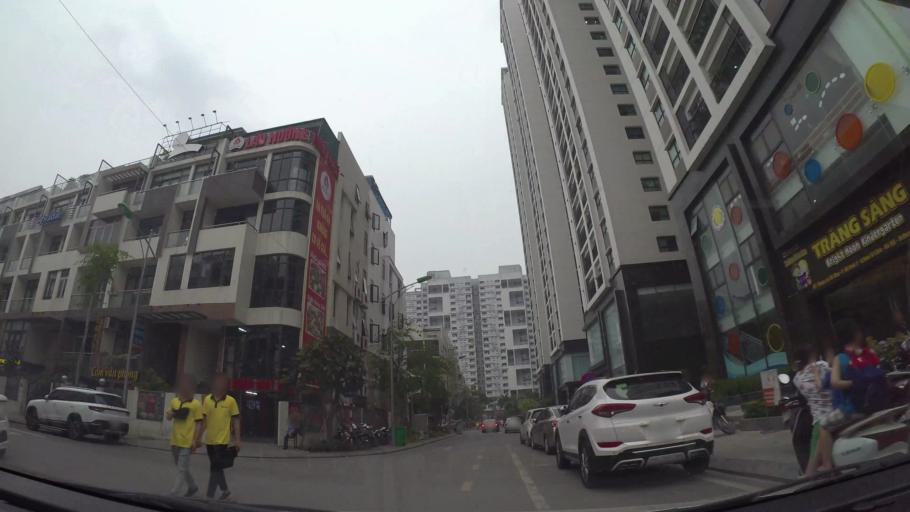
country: VN
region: Ha Noi
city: Cau Dien
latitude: 21.0360
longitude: 105.7674
